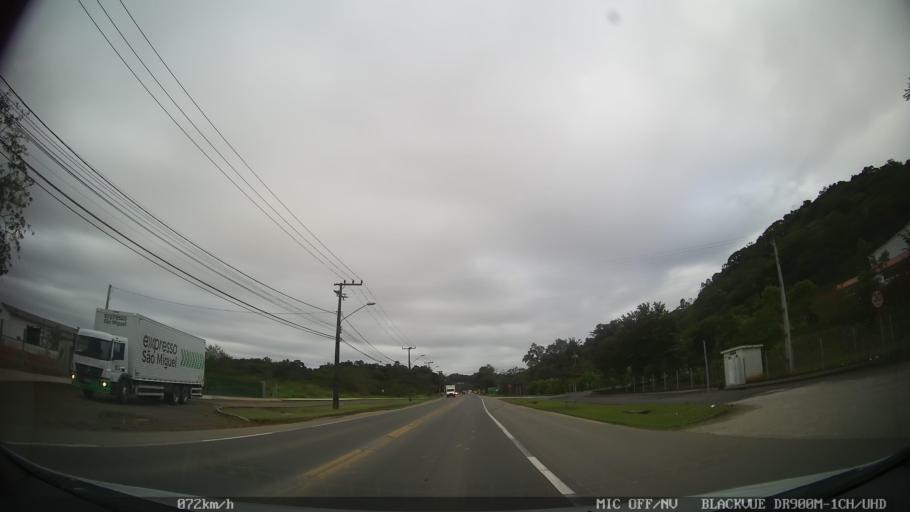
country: BR
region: Santa Catarina
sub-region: Joinville
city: Joinville
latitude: -26.2766
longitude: -48.9238
